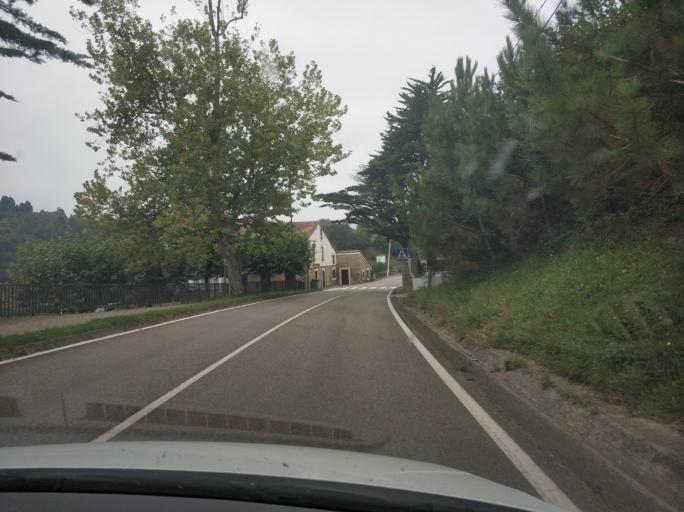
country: ES
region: Cantabria
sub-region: Provincia de Cantabria
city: Comillas
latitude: 43.3793
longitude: -4.3167
